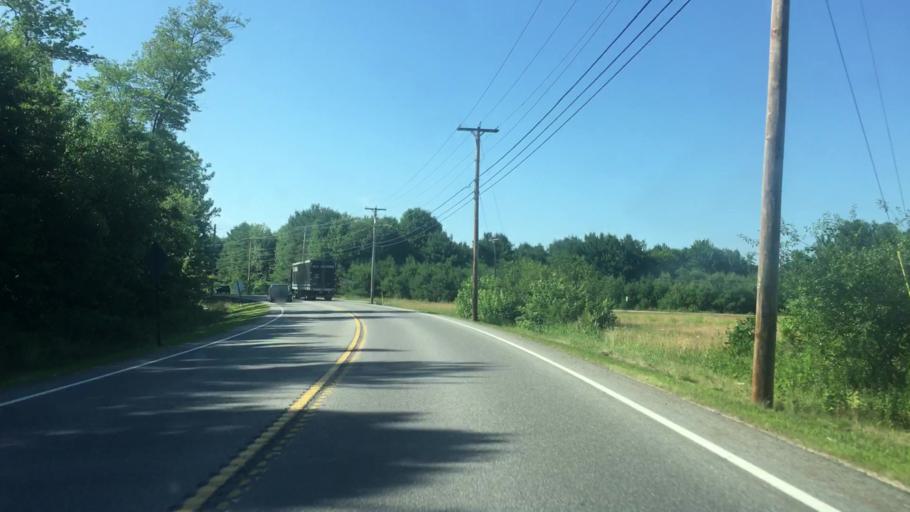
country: US
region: Maine
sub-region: York County
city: Buxton
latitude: 43.5624
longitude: -70.4983
